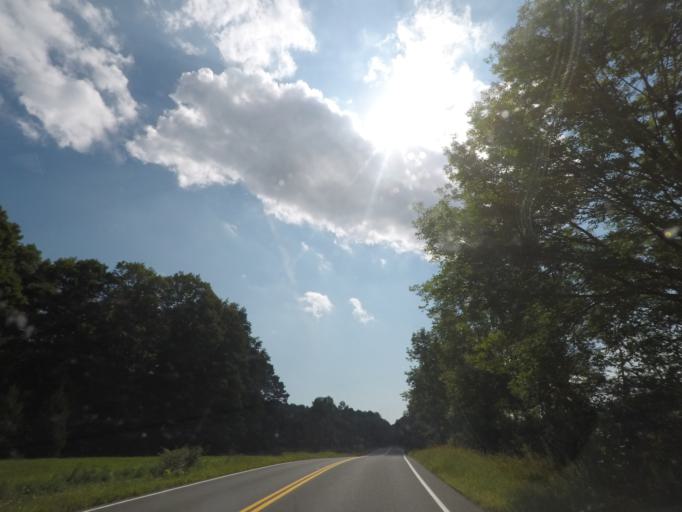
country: US
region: New York
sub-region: Rensselaer County
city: Poestenkill
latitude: 42.7769
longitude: -73.5372
